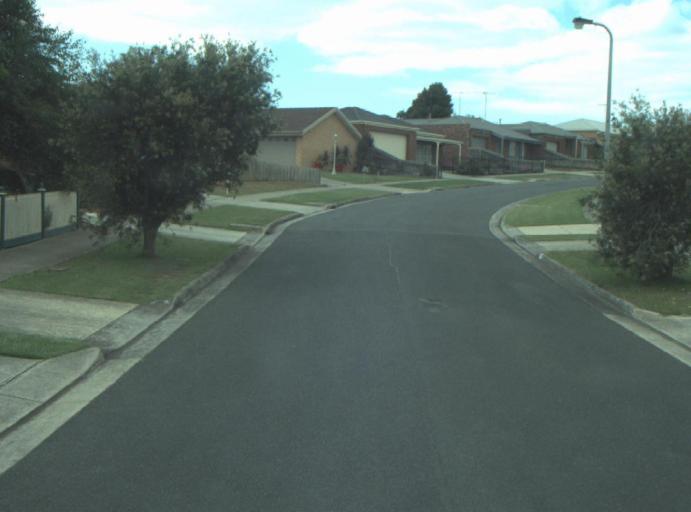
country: AU
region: Victoria
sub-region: Greater Geelong
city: Wandana Heights
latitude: -38.2013
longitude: 144.3233
